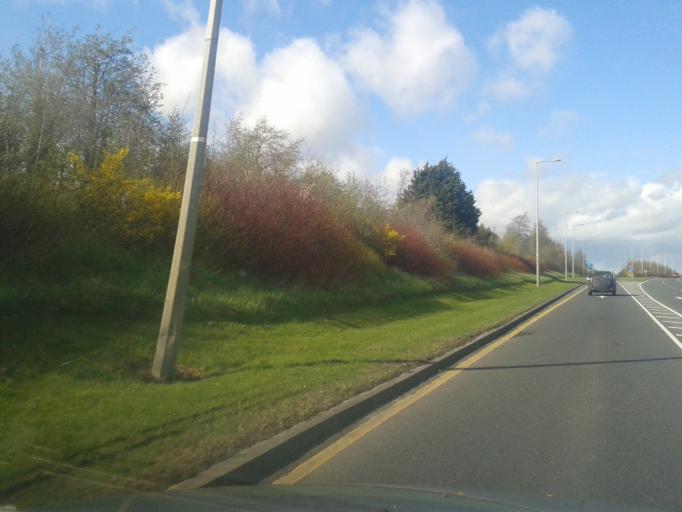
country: IE
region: Leinster
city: Beaumont
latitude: 53.3905
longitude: -6.2420
